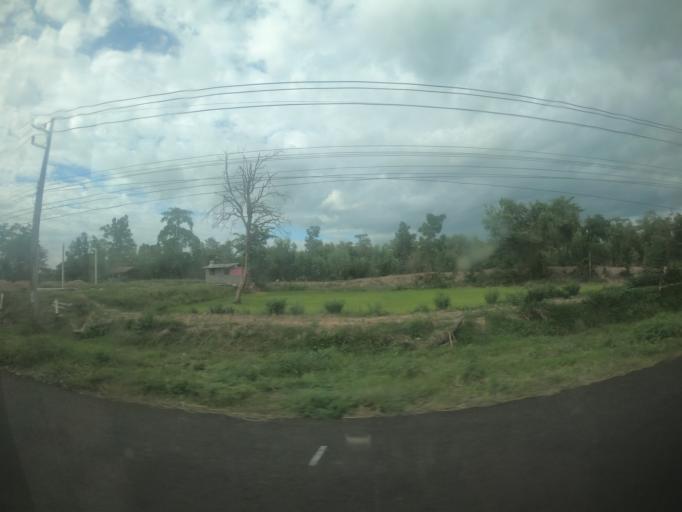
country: TH
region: Surin
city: Prasat
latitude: 14.5683
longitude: 103.4905
